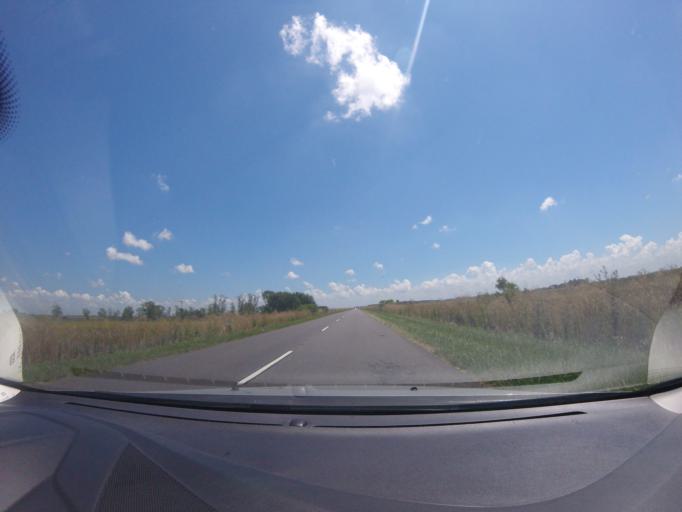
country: AR
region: Buenos Aires
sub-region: Partido de Las Flores
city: Las Flores
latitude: -36.2700
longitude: -59.0434
